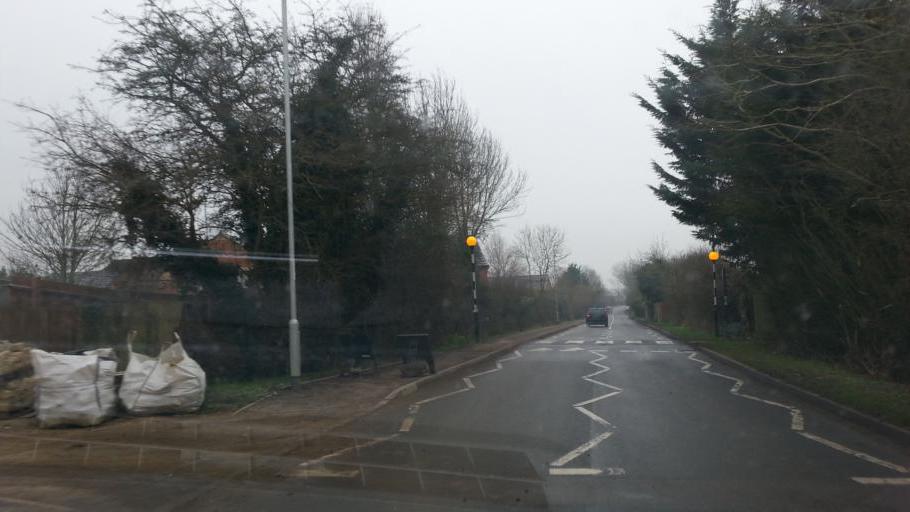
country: GB
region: England
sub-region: Northamptonshire
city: Brackley
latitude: 52.0422
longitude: -1.1516
